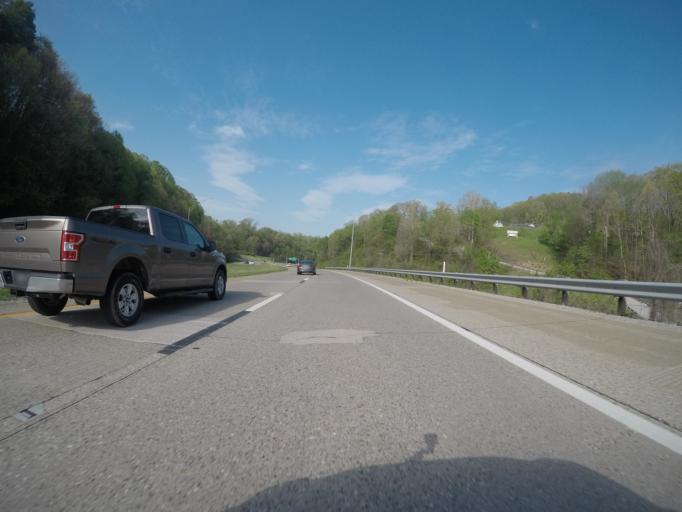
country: US
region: West Virginia
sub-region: Kanawha County
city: South Charleston
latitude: 38.3399
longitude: -81.6879
